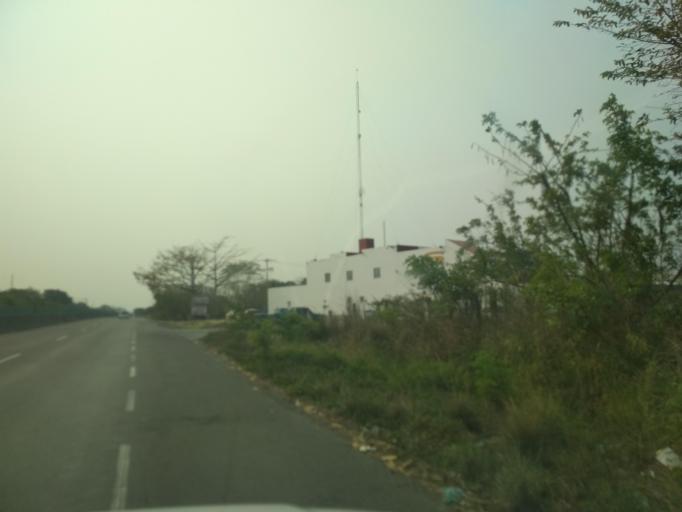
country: MX
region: Veracruz
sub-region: Veracruz
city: Las Amapolas
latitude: 19.1240
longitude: -96.2401
